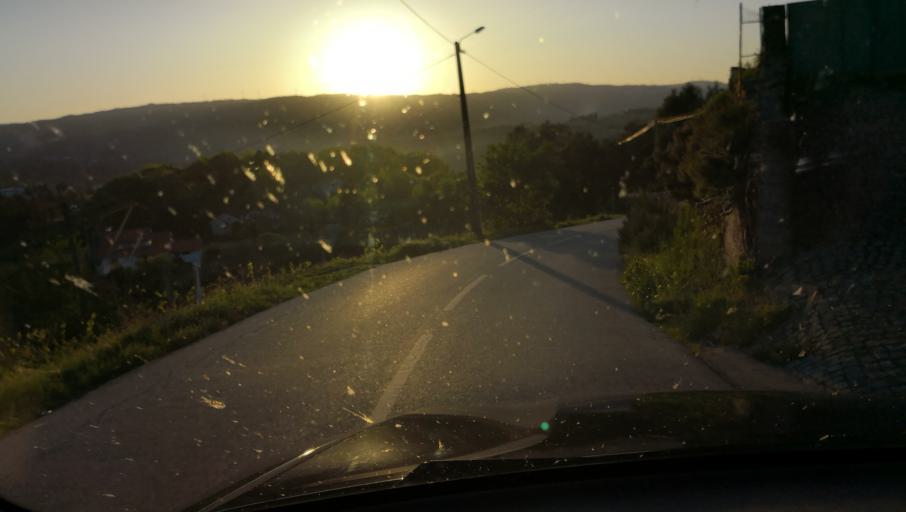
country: PT
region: Vila Real
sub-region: Mondim de Basto
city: Mondim de Basto
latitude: 41.4093
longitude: -7.9459
